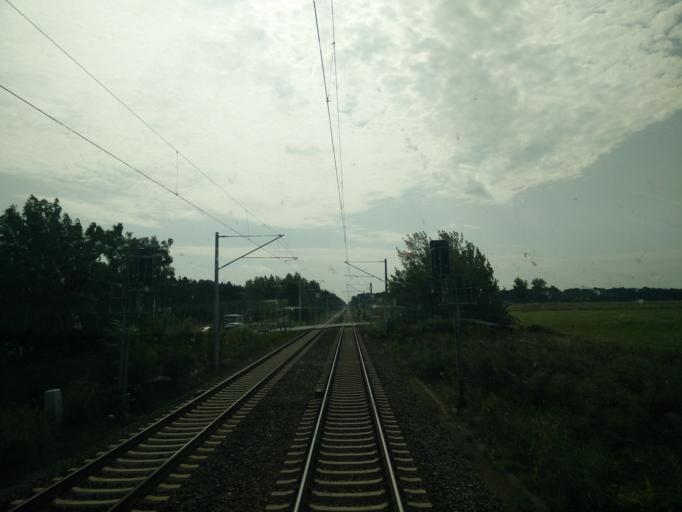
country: DE
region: Brandenburg
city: Luebben
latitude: 51.9204
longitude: 13.8948
